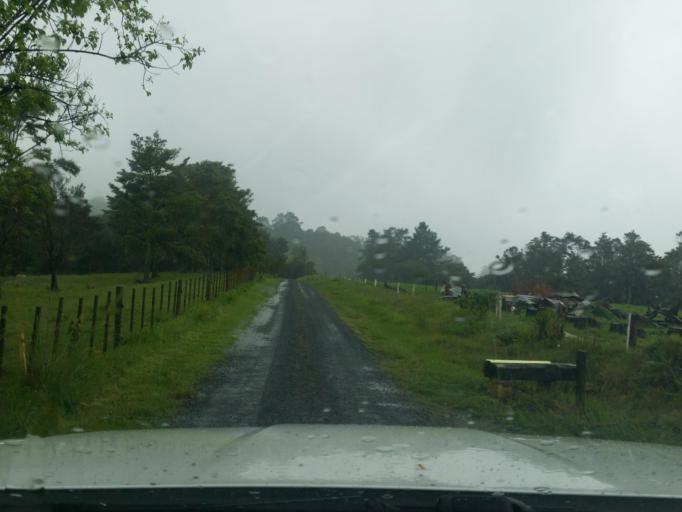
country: NZ
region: Northland
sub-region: Kaipara District
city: Dargaville
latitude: -35.8620
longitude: 174.0169
